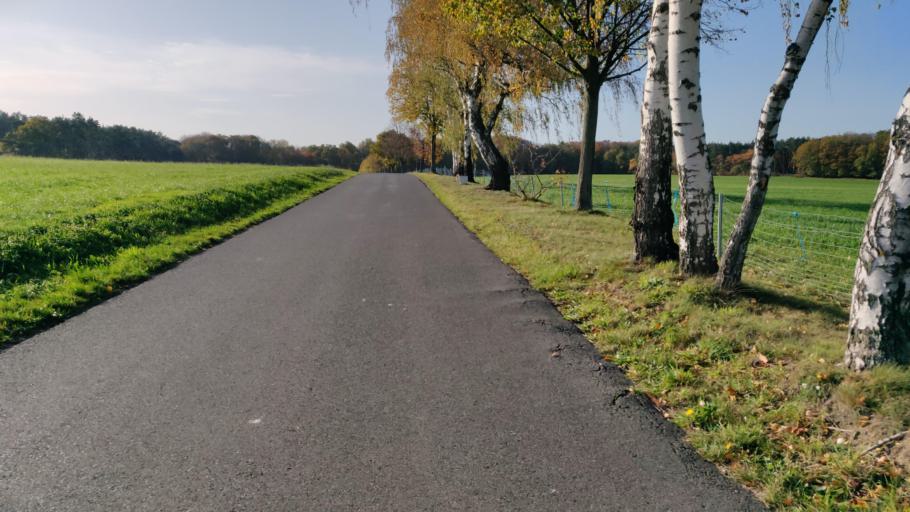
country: DE
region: Brandenburg
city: Ortrand
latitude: 51.3454
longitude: 13.7540
